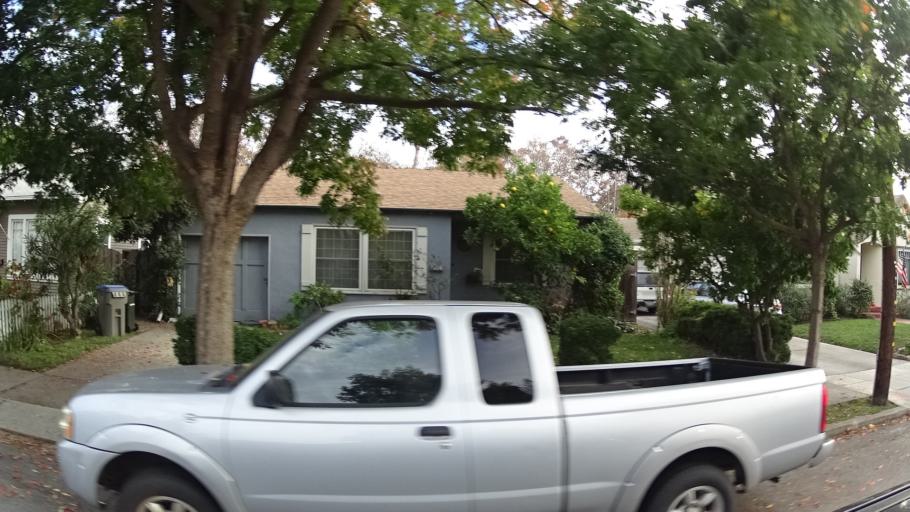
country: US
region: California
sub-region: Santa Clara County
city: Buena Vista
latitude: 37.3303
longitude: -121.9187
